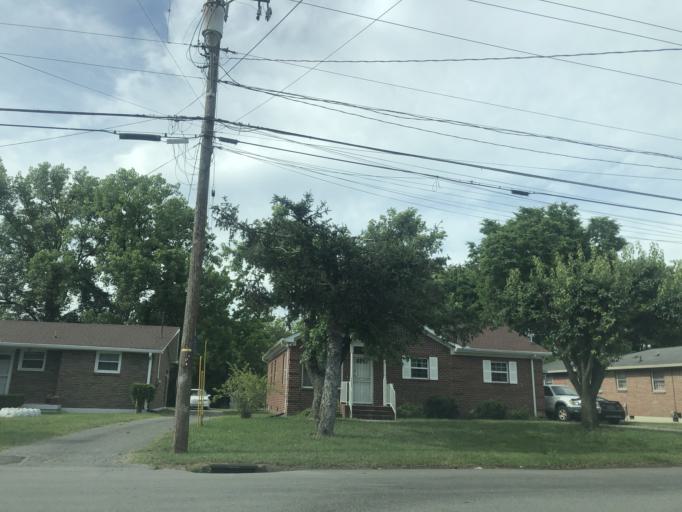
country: US
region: Tennessee
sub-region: Davidson County
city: Nashville
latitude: 36.2195
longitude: -86.8151
